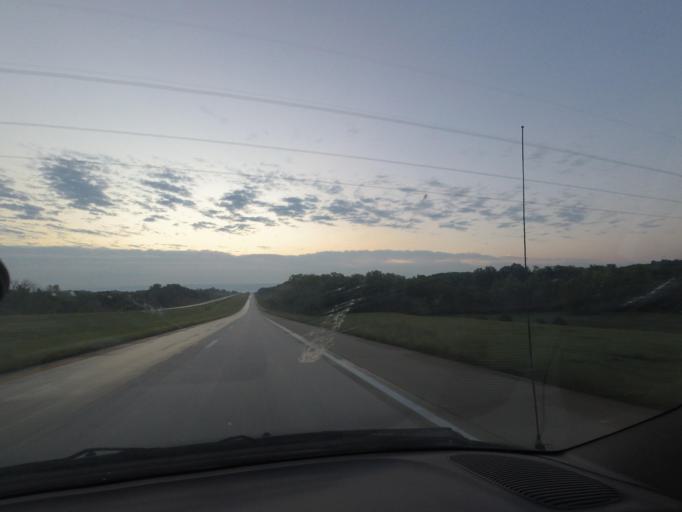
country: US
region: Missouri
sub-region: Macon County
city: Macon
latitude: 39.7590
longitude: -92.6619
